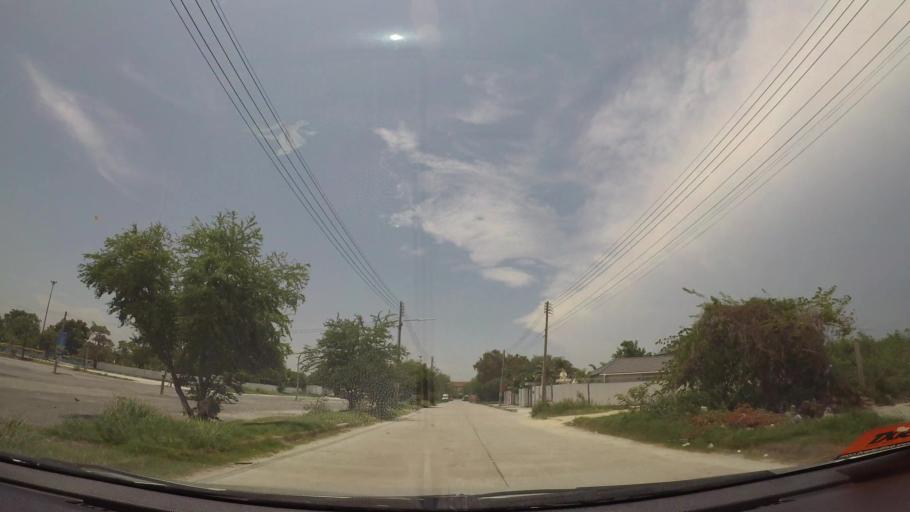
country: TH
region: Chon Buri
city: Chon Buri
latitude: 13.3417
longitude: 100.9478
